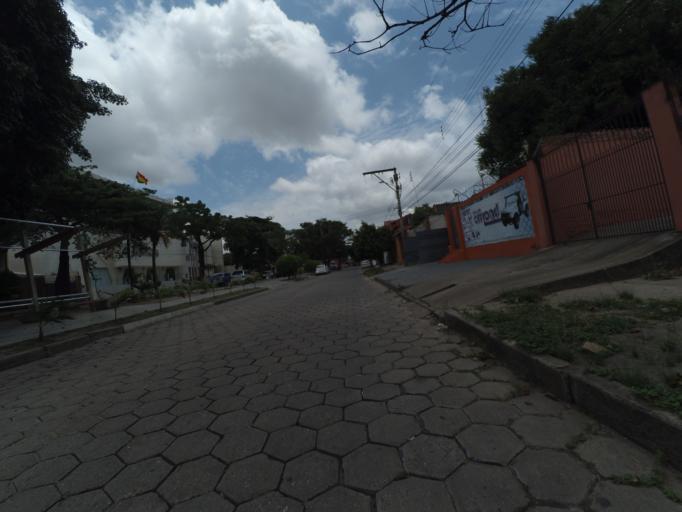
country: BO
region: Santa Cruz
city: Santa Cruz de la Sierra
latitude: -17.7993
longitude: -63.2003
